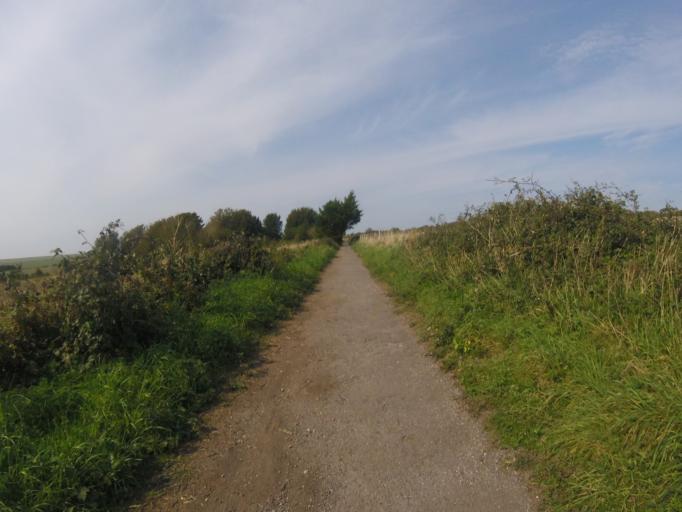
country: GB
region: England
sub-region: West Sussex
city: Fulking
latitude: 50.8717
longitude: -0.1996
